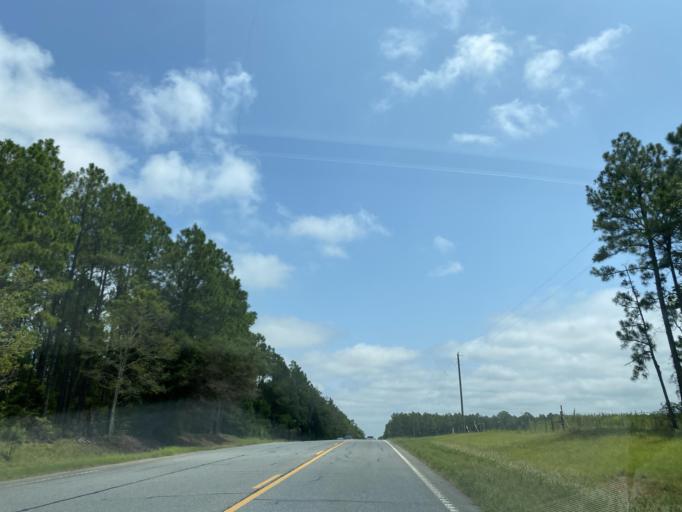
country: US
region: Georgia
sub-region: Wheeler County
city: Alamo
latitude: 32.1151
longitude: -82.8085
